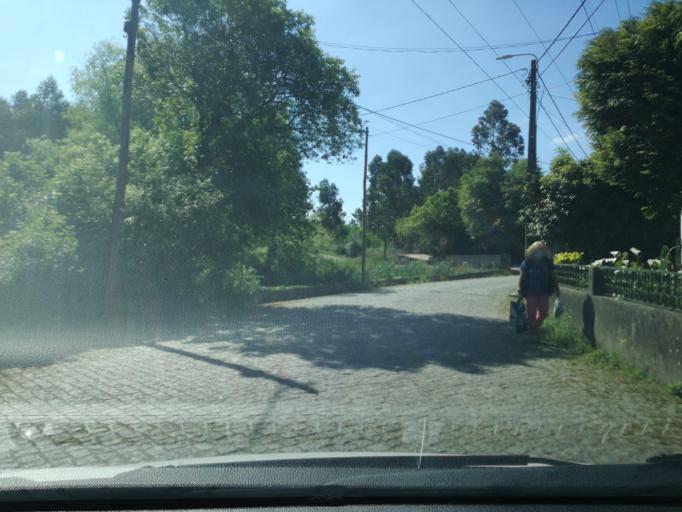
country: PT
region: Porto
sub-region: Maia
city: Nogueira
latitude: 41.2490
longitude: -8.6023
